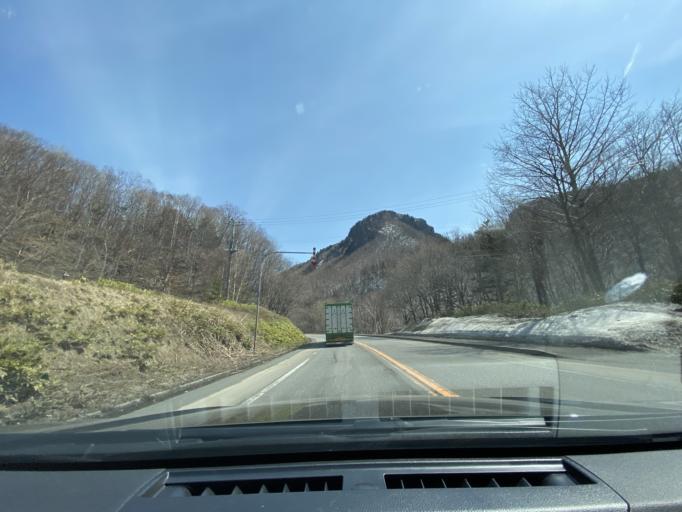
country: JP
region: Hokkaido
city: Kamikawa
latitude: 43.7265
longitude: 142.9559
